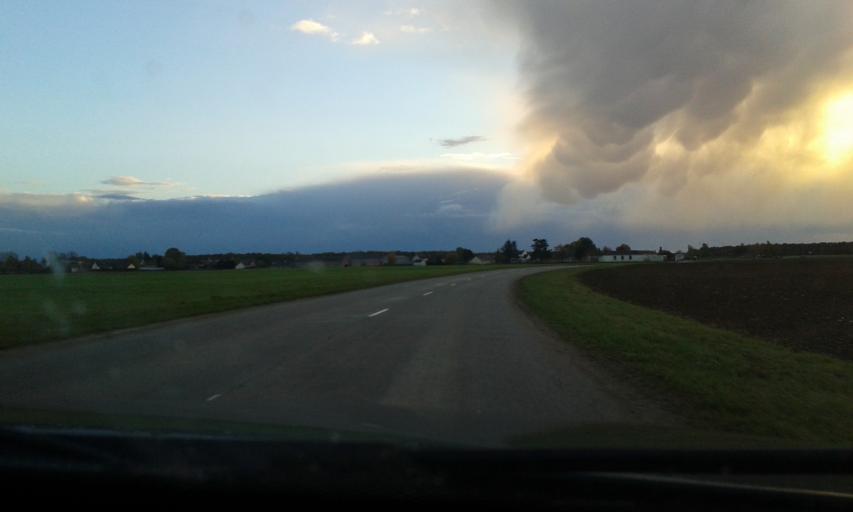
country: FR
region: Centre
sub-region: Departement du Loiret
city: Bricy
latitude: 47.9741
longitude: 1.7813
